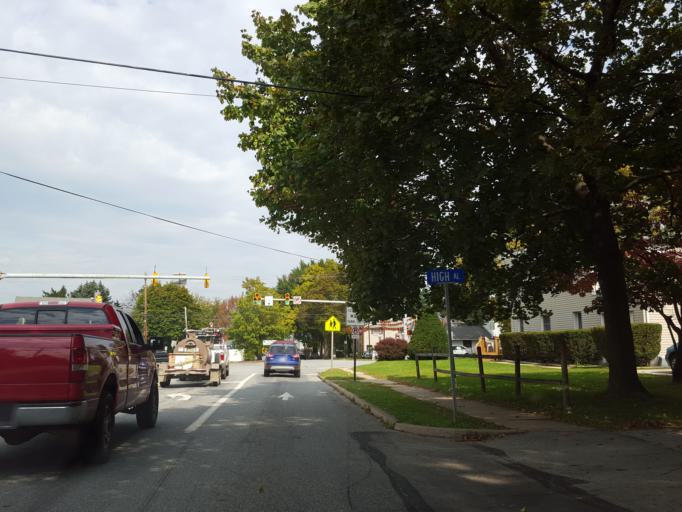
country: US
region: Pennsylvania
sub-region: York County
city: East York
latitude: 39.9670
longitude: -76.6999
